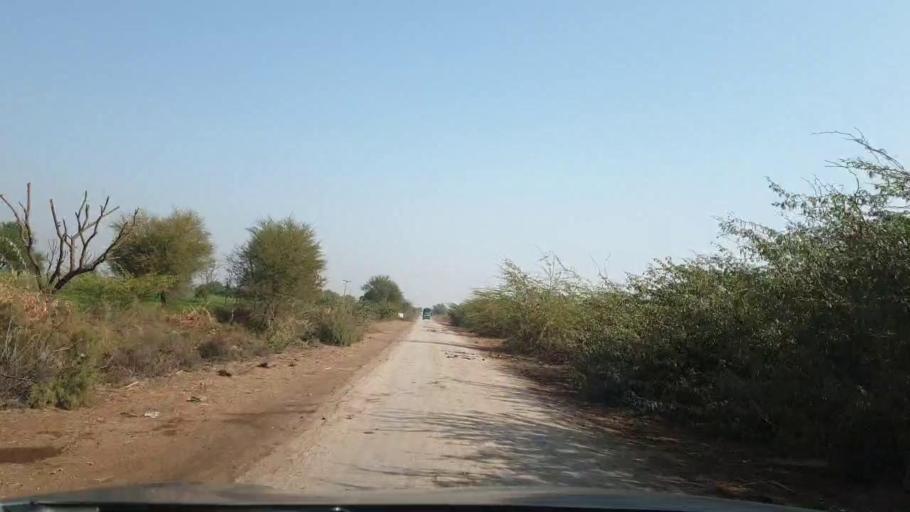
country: PK
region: Sindh
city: Berani
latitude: 25.6200
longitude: 68.8531
